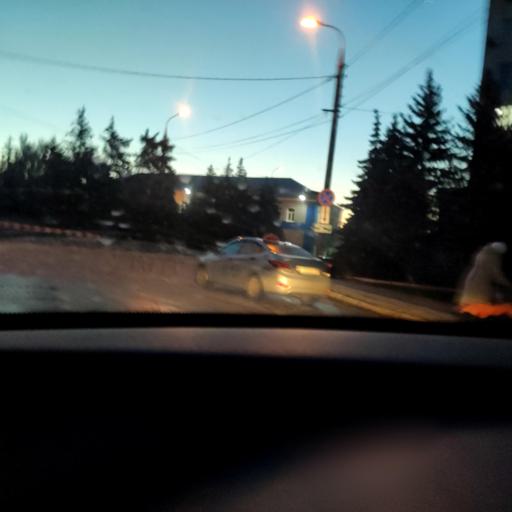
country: RU
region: Samara
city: Samara
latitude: 53.1963
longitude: 50.2230
